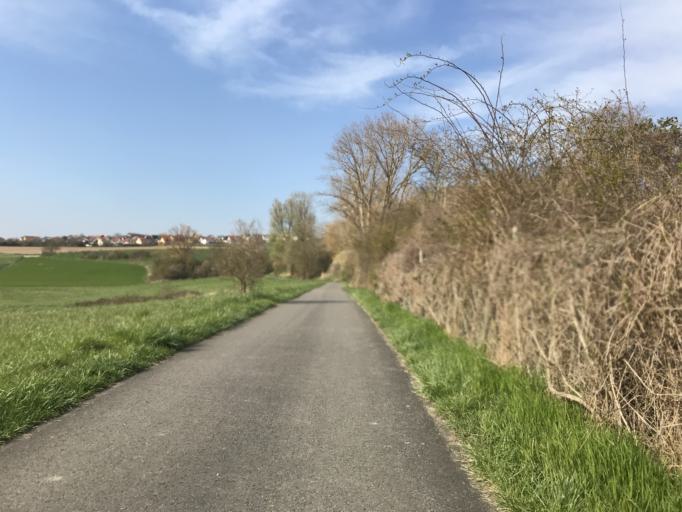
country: DE
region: Rheinland-Pfalz
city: Schwabenheim
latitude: 49.9202
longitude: 8.1044
